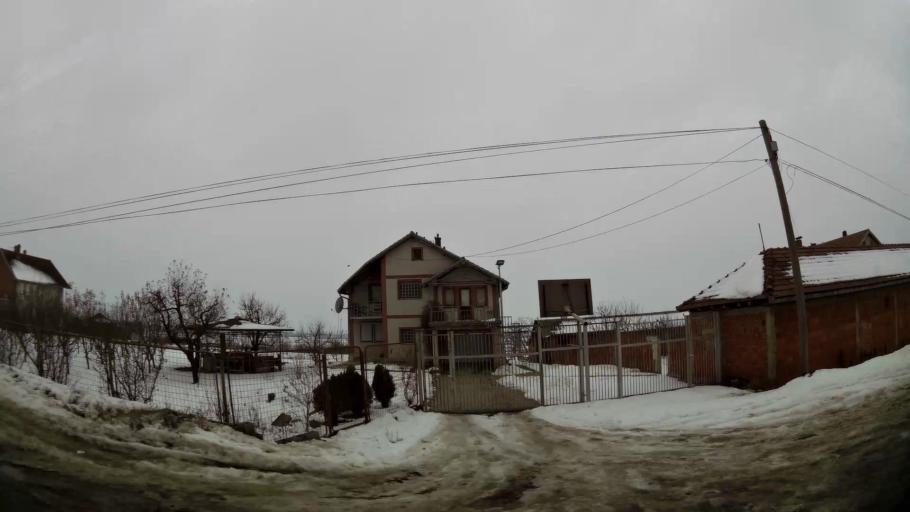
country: XK
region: Pristina
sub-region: Komuna e Prishtines
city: Pristina
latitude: 42.7287
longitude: 21.1438
